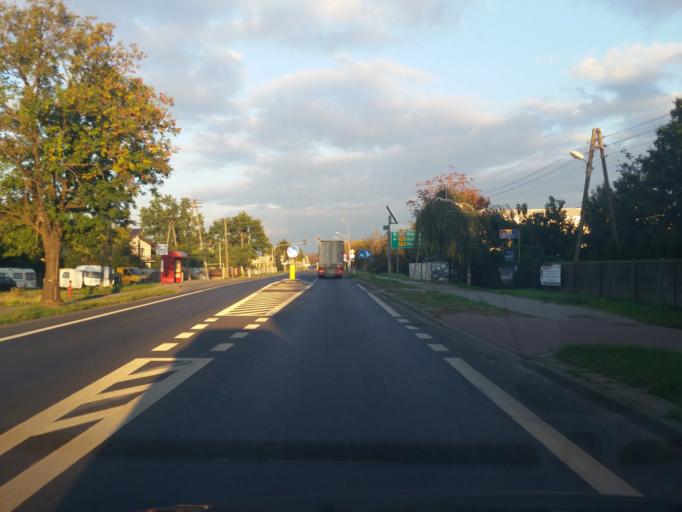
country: PL
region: Masovian Voivodeship
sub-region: Powiat warszawski zachodni
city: Ozarow Mazowiecki
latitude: 52.2111
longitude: 20.7679
